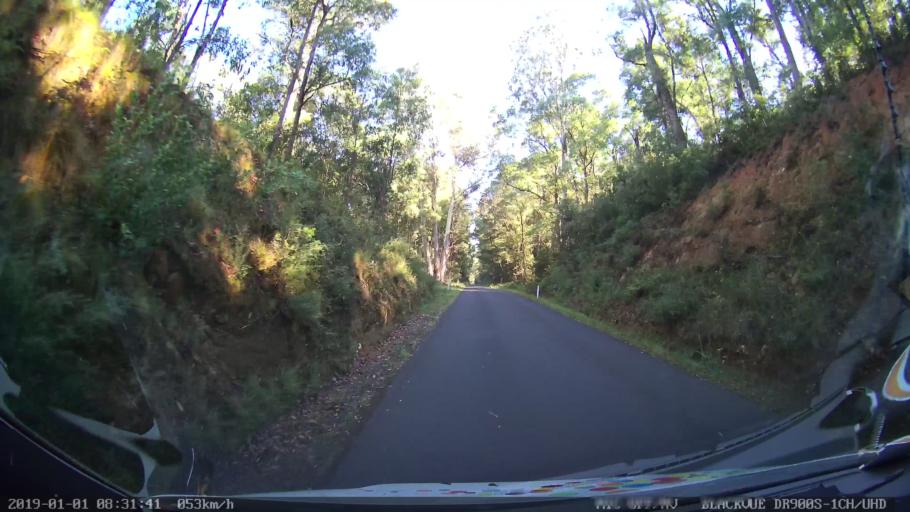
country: AU
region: New South Wales
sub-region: Snowy River
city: Jindabyne
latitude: -36.3682
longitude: 148.2053
